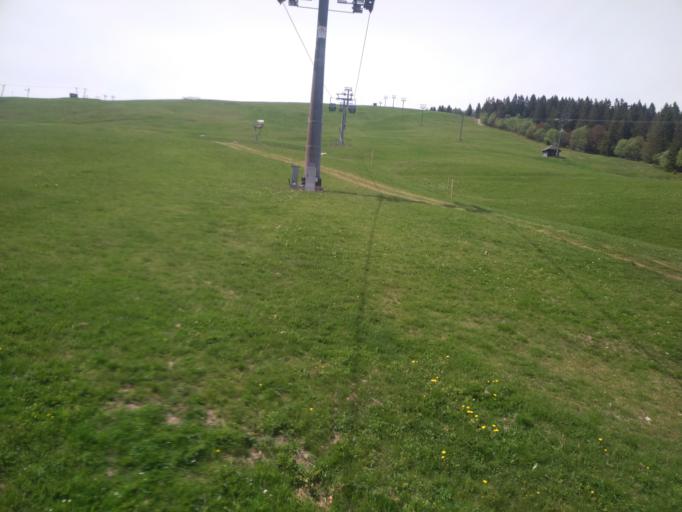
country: DE
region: Baden-Wuerttemberg
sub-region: Freiburg Region
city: Bernau
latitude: 47.8625
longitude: 8.0360
